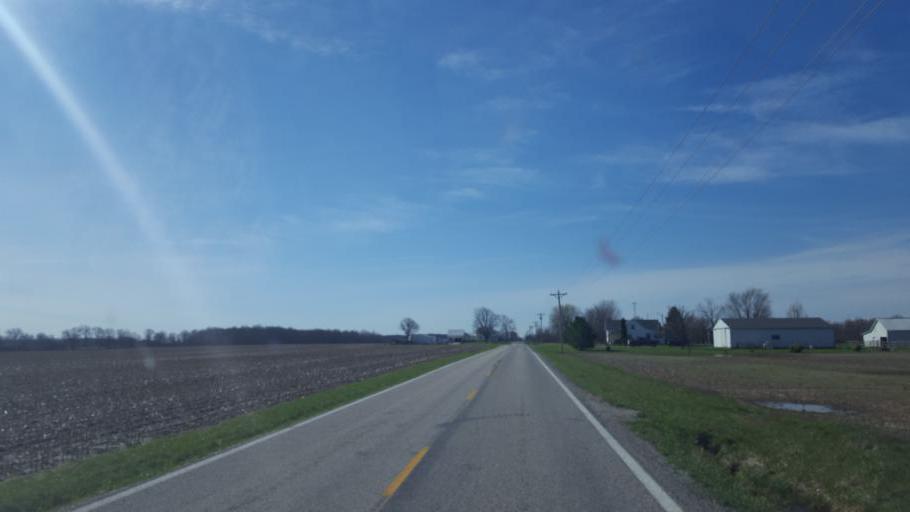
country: US
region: Ohio
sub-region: Morrow County
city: Cardington
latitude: 40.5718
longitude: -82.9622
